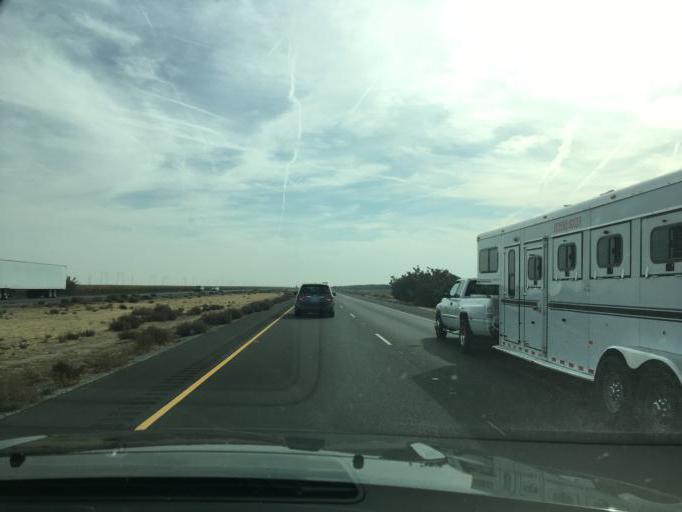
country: US
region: California
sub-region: Kings County
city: Kettleman City
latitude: 35.9207
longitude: -119.8981
